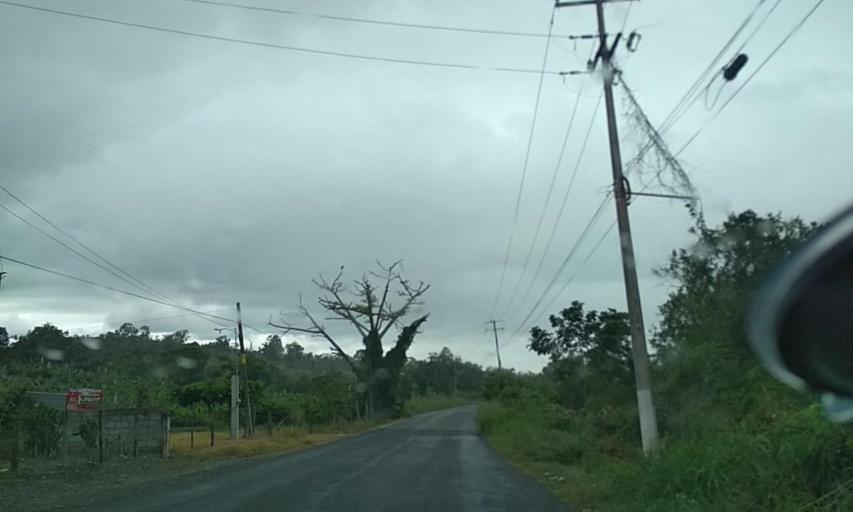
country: MX
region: Veracruz
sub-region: Papantla
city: Residencial Tajin
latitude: 20.6369
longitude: -97.3696
